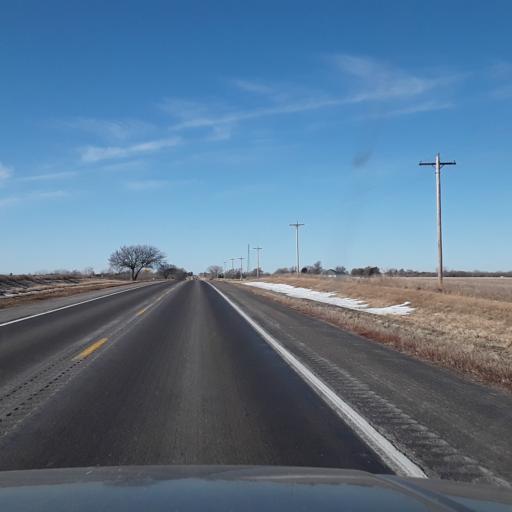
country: US
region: Nebraska
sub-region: Adams County
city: Hastings
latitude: 40.5681
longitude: -98.4877
